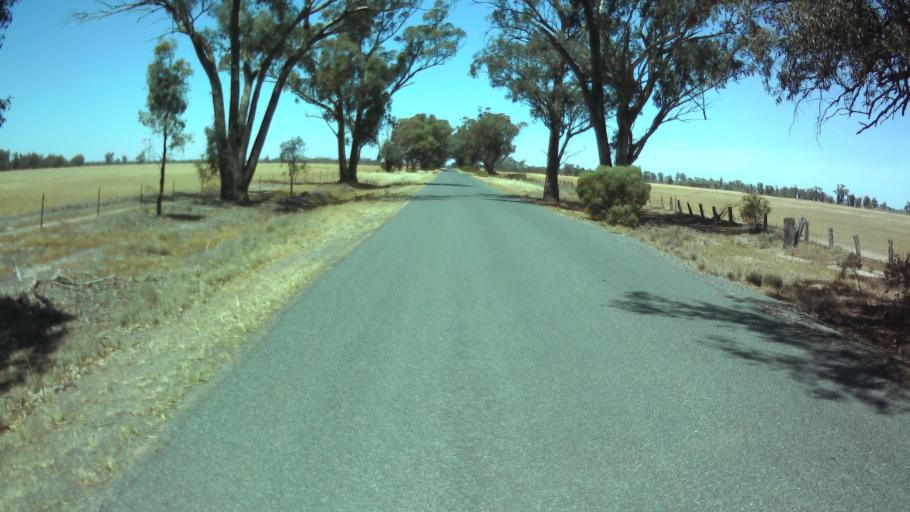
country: AU
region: New South Wales
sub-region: Weddin
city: Grenfell
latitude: -34.0197
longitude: 147.7929
